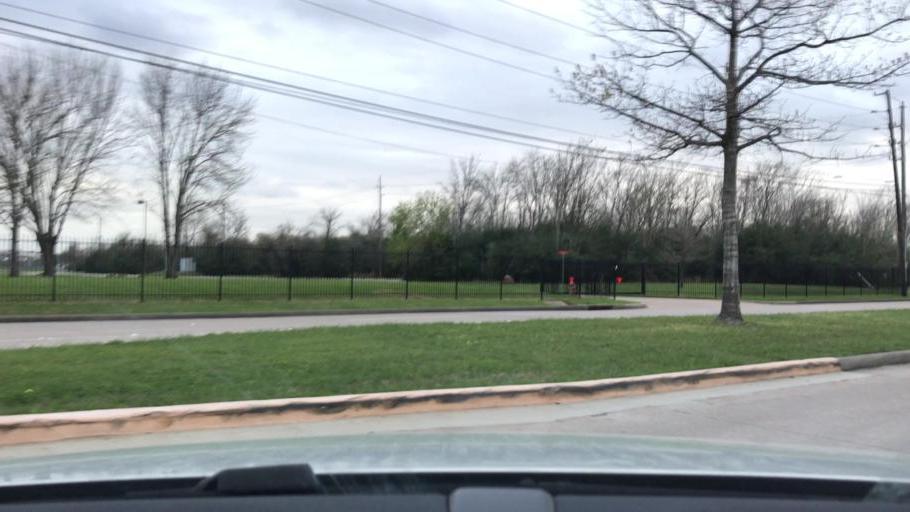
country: US
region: Texas
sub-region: Harris County
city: Katy
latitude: 29.8020
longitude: -95.7725
